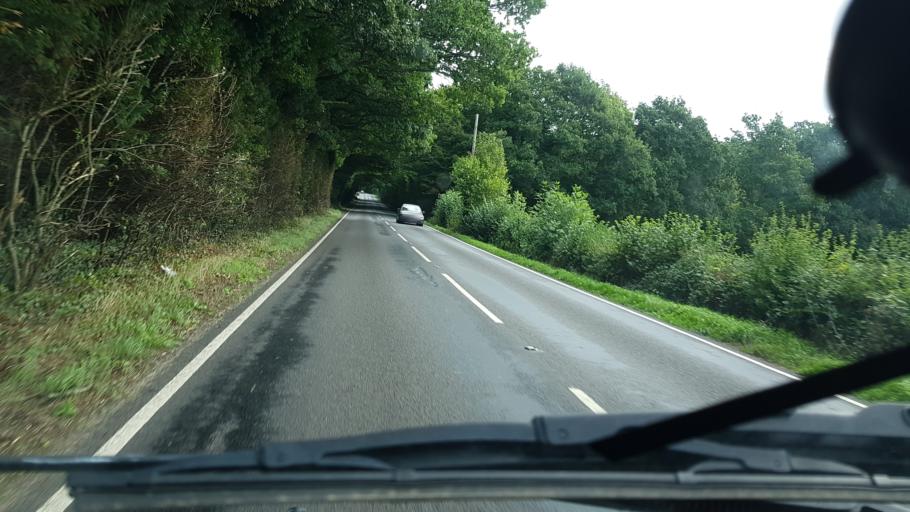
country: GB
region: England
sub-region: West Sussex
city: Rudgwick
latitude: 51.0880
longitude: -0.3967
